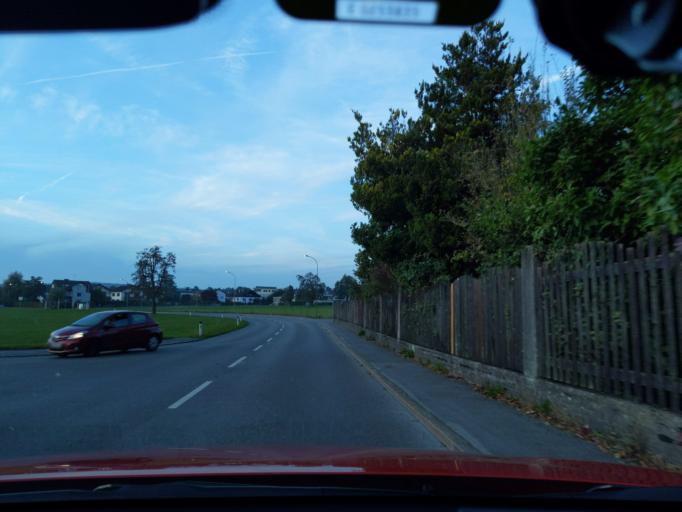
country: AT
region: Vorarlberg
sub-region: Politischer Bezirk Bregenz
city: Lochau
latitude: 47.5365
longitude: 9.7451
